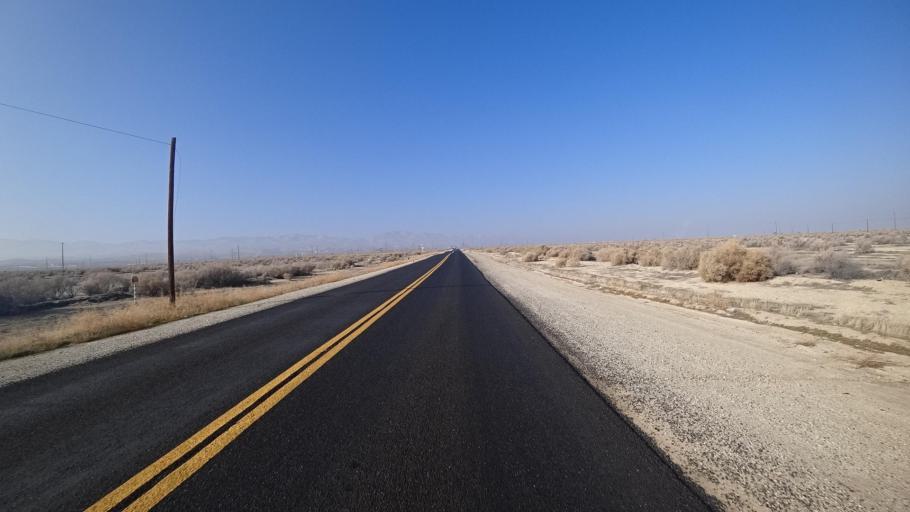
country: US
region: California
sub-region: Kern County
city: Taft Heights
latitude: 35.1804
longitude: -119.5199
